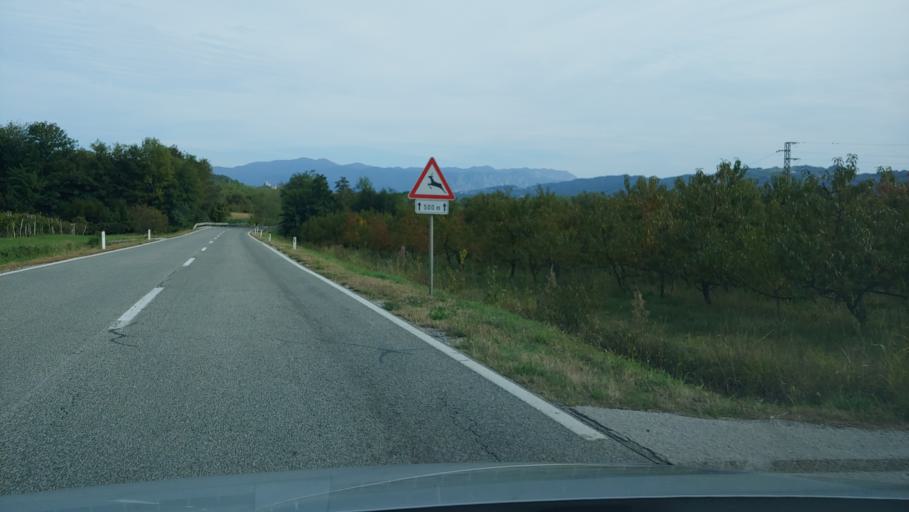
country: SI
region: Ajdovscina
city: Lokavec
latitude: 45.8878
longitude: 13.8257
